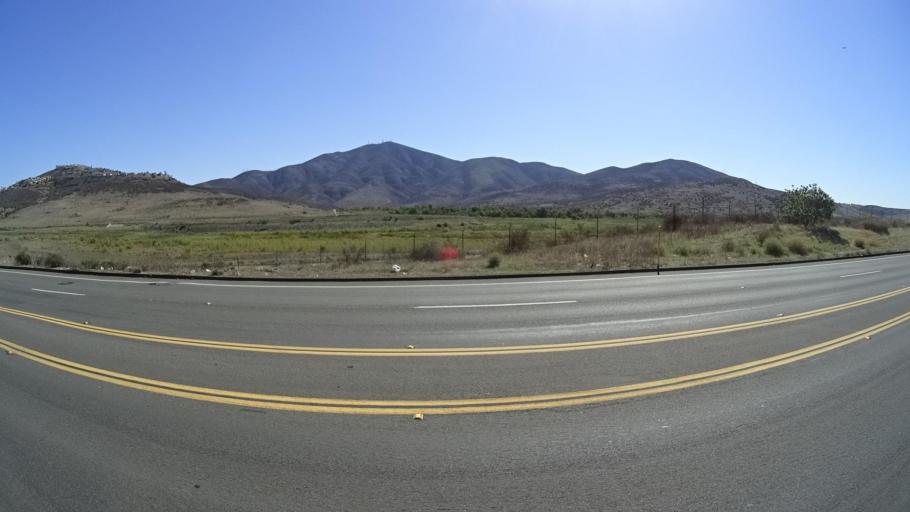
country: US
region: California
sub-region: San Diego County
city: La Presa
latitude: 32.7121
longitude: -116.9816
